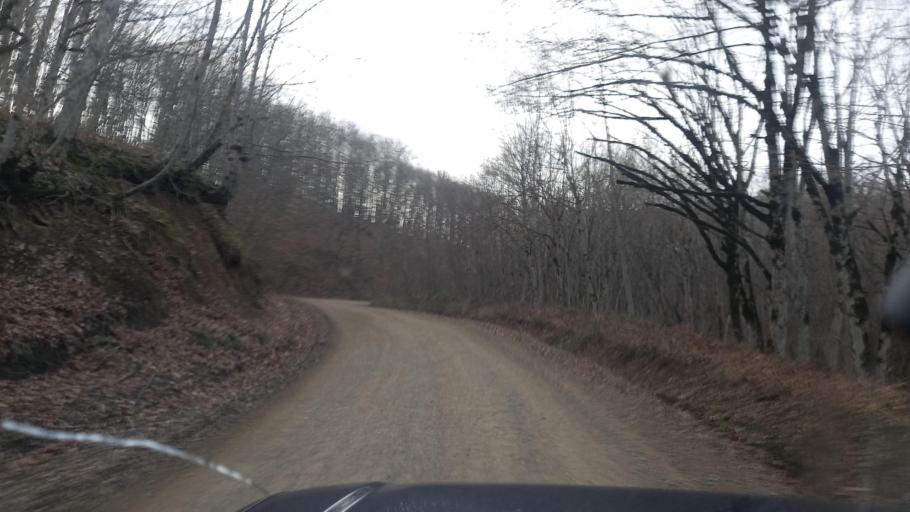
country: RU
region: Krasnodarskiy
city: Agoy
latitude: 44.3617
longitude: 39.2204
